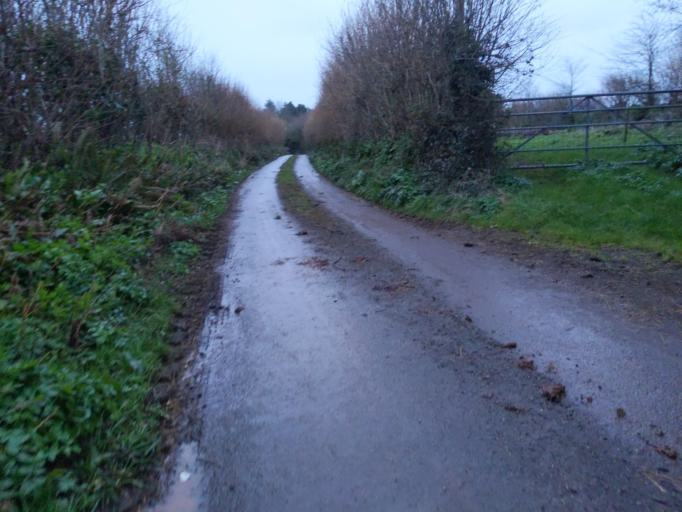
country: GB
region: England
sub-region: Devon
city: Yealmpton
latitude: 50.3258
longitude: -4.0278
